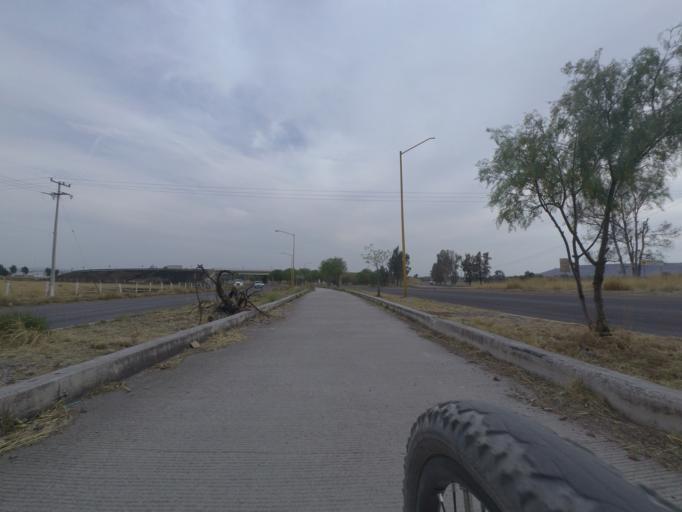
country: MX
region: Aguascalientes
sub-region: Aguascalientes
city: La Loma de los Negritos
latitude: 21.8649
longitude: -102.3717
